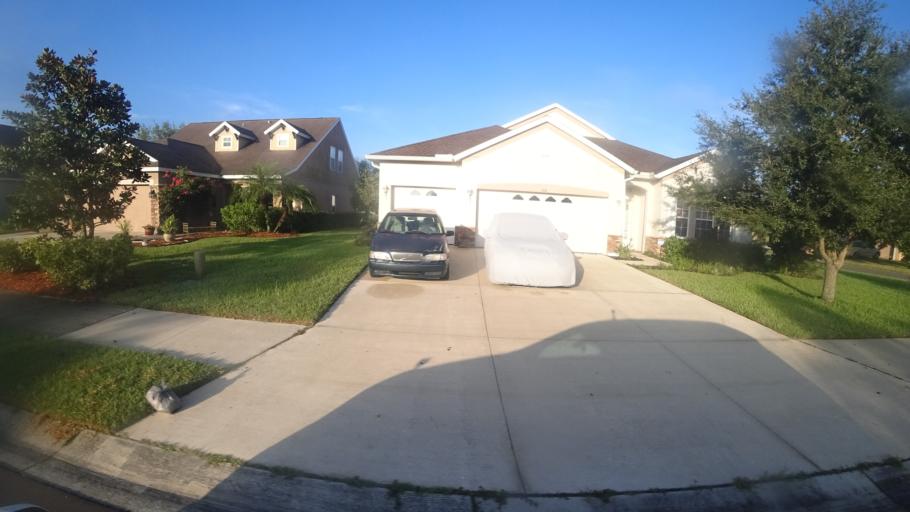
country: US
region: Florida
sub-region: Manatee County
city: Ellenton
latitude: 27.5346
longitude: -82.4126
